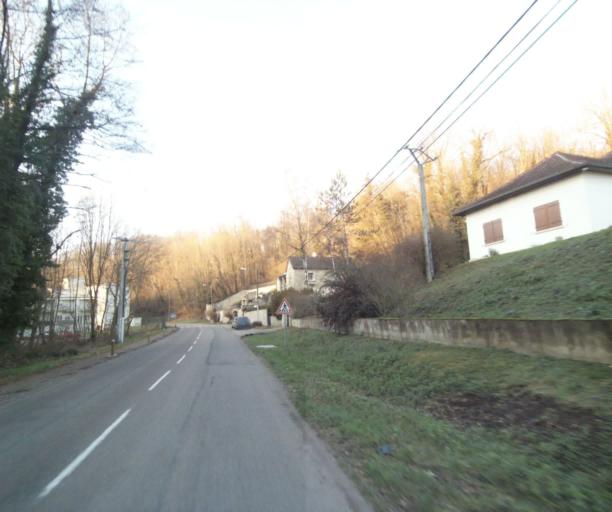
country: FR
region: Champagne-Ardenne
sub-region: Departement de la Haute-Marne
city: Bienville
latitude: 48.6103
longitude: 5.0507
